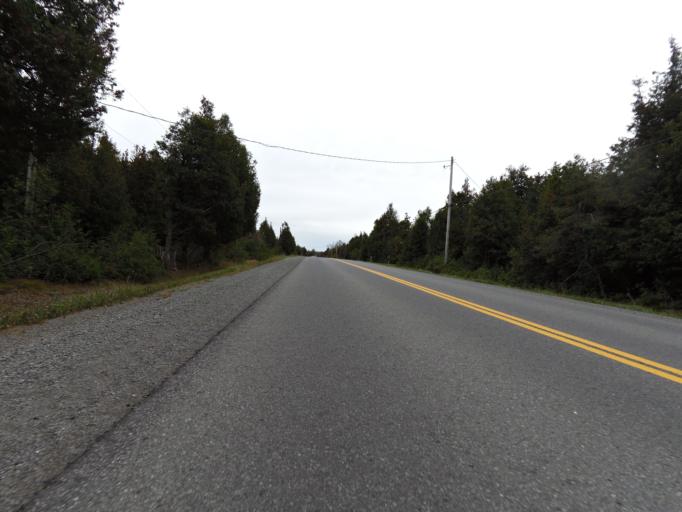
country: CA
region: Ontario
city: Brockville
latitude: 44.7837
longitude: -75.7632
